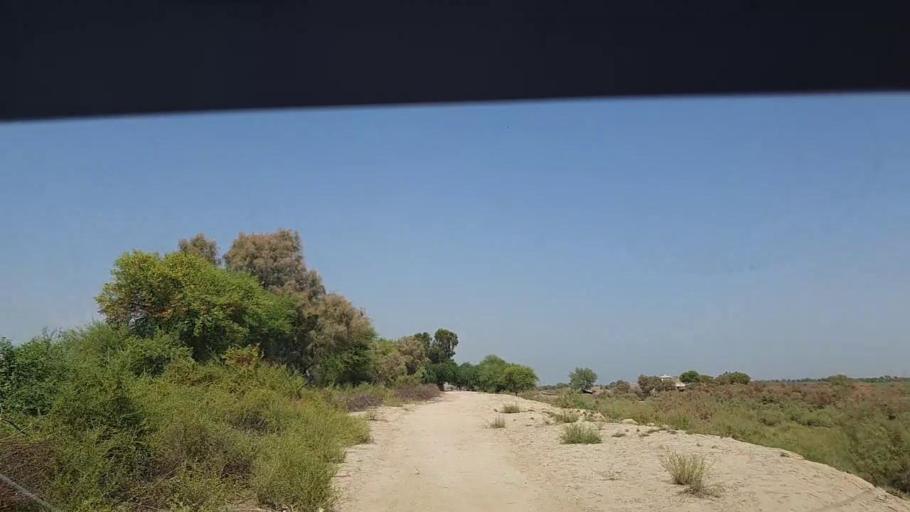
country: PK
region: Sindh
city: Kandhkot
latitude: 28.1783
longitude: 69.1508
